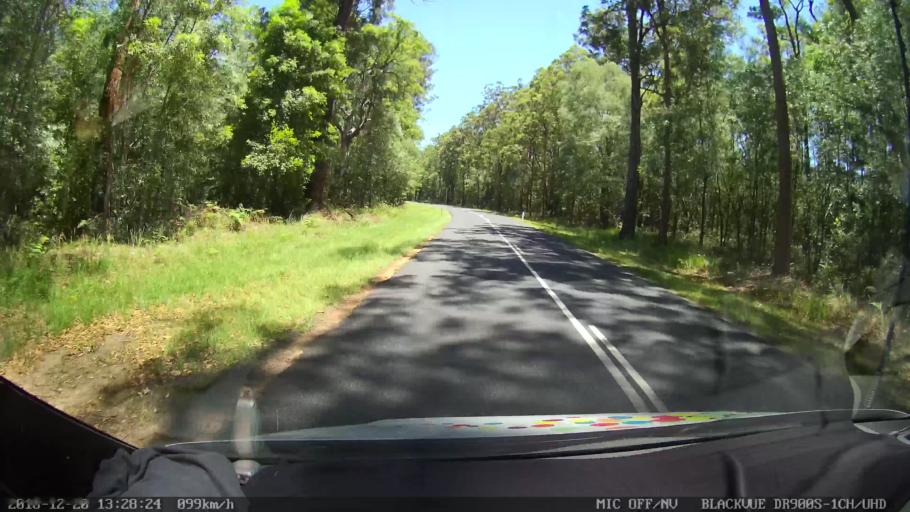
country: AU
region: New South Wales
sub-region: Clarence Valley
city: Gordon
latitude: -29.1741
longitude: 152.9903
